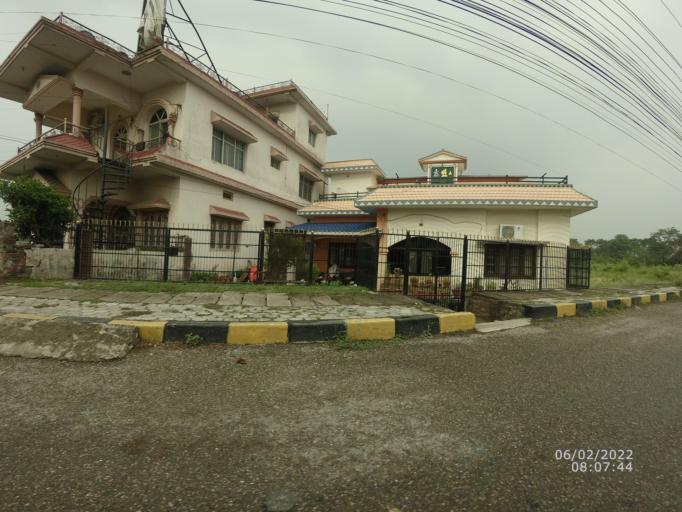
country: NP
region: Western Region
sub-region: Lumbini Zone
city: Bhairahawa
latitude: 27.4842
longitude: 83.4615
